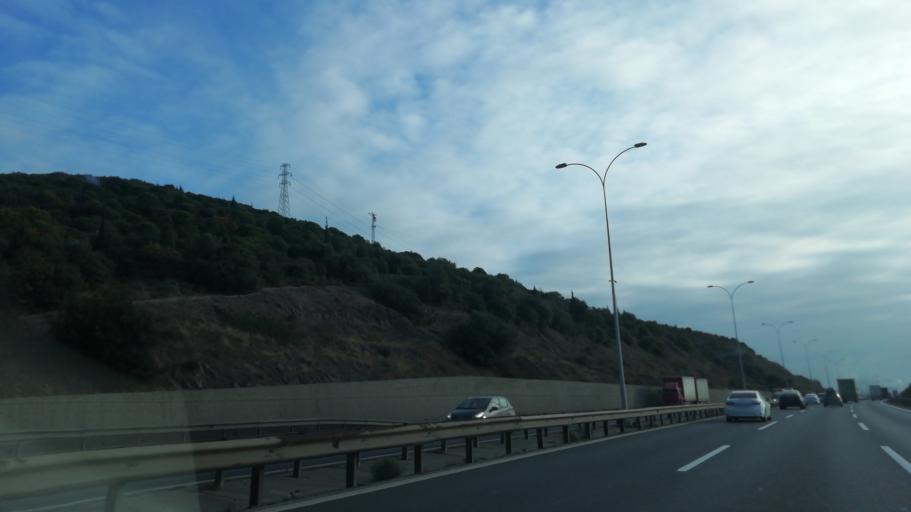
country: TR
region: Kocaeli
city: Hereke
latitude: 40.7799
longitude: 29.6686
